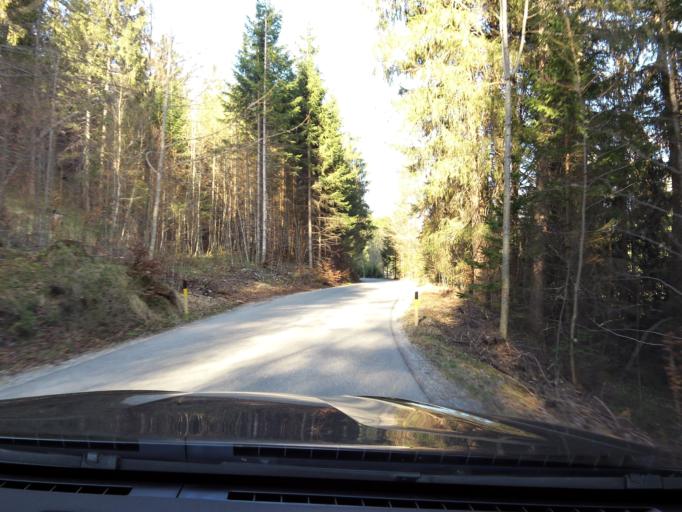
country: DE
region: Bavaria
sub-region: Upper Bavaria
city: Wallgau
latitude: 47.5262
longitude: 11.2908
